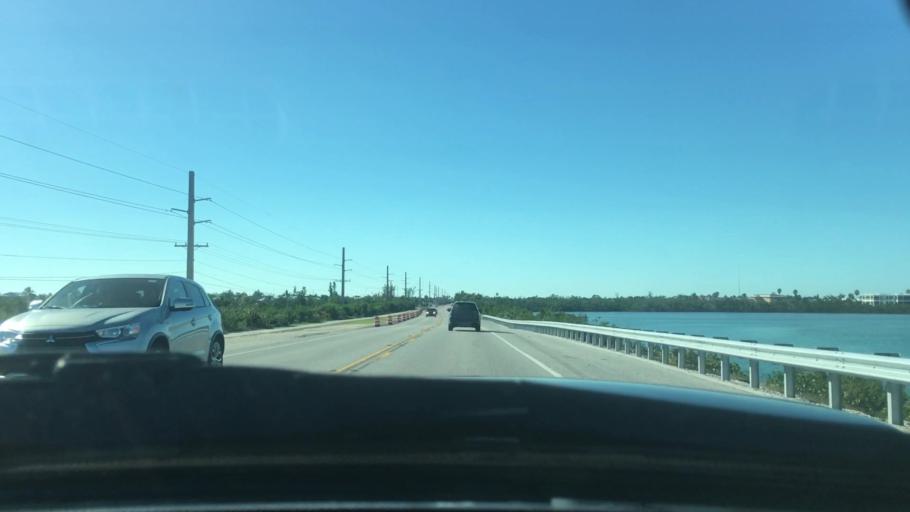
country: US
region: Florida
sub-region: Monroe County
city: Cudjoe Key
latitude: 24.6627
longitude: -81.4683
